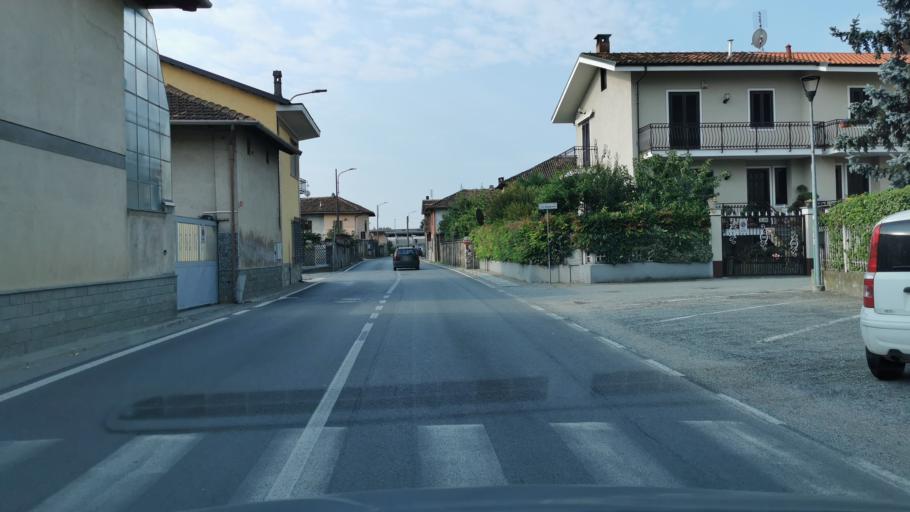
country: IT
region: Piedmont
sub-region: Provincia di Torino
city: Scalenghe
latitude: 44.8872
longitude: 7.4958
